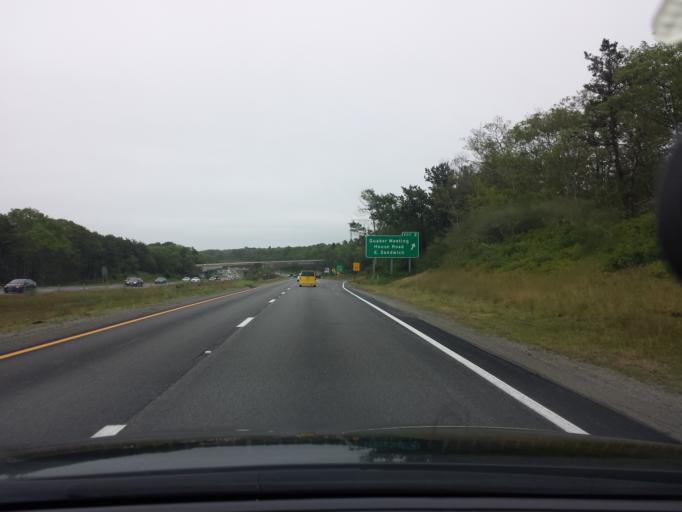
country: US
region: Massachusetts
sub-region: Barnstable County
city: East Sandwich
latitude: 41.7320
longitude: -70.4608
